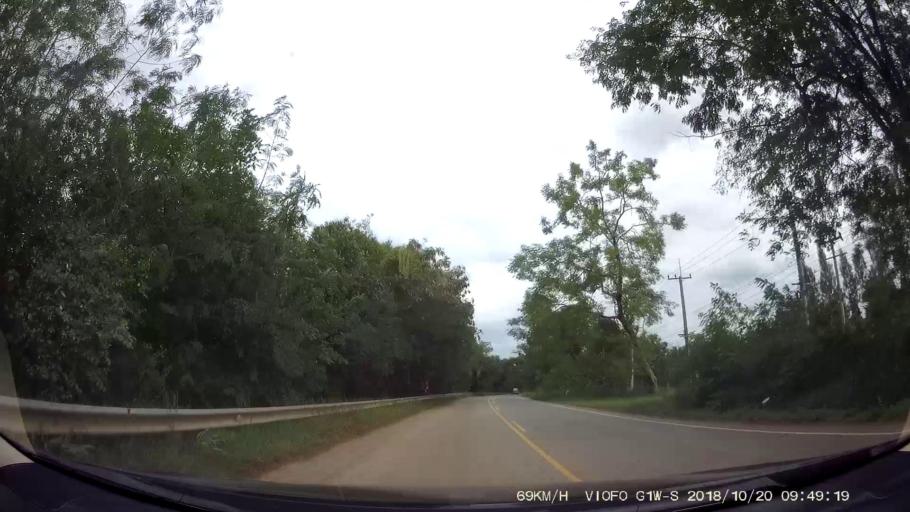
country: TH
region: Chaiyaphum
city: Khon San
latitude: 16.5182
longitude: 101.9057
